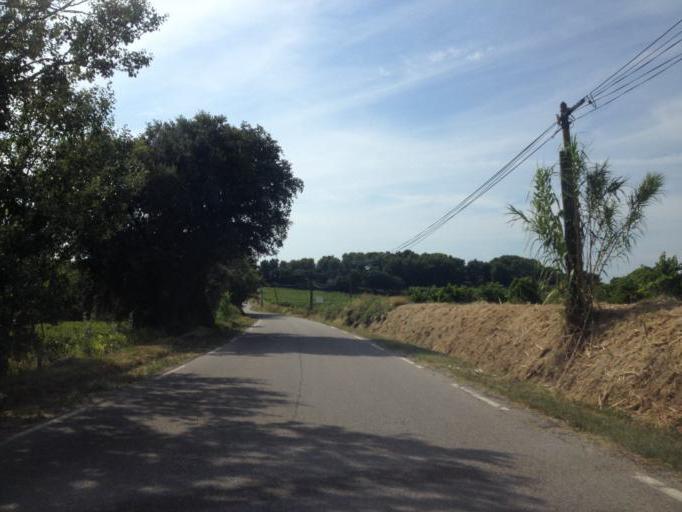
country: FR
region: Provence-Alpes-Cote d'Azur
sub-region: Departement du Vaucluse
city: Vacqueyras
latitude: 44.1381
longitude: 4.9984
